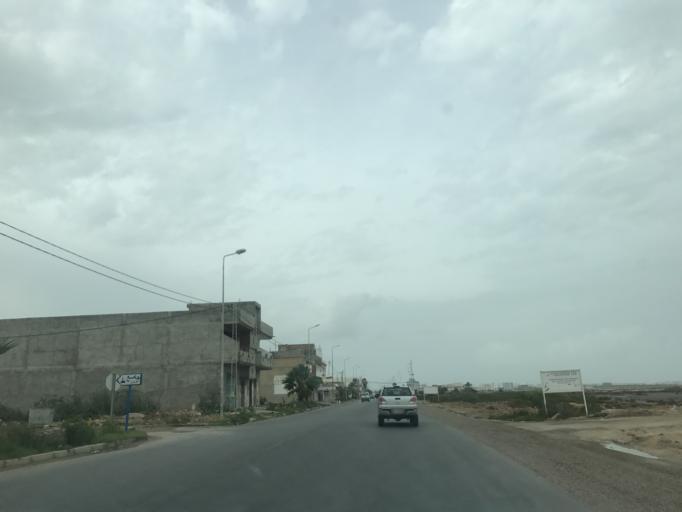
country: TN
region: Al Munastir
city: Banbalah
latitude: 35.7065
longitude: 10.8240
